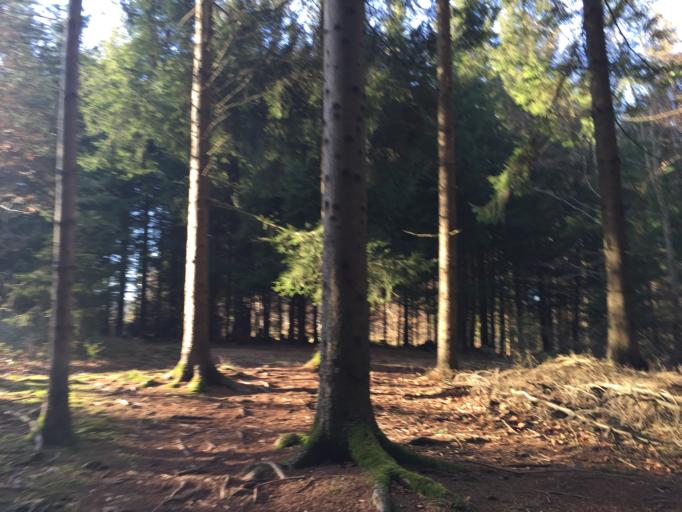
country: CH
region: Bern
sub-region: Bern-Mittelland District
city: Koniz
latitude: 46.9332
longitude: 7.4111
